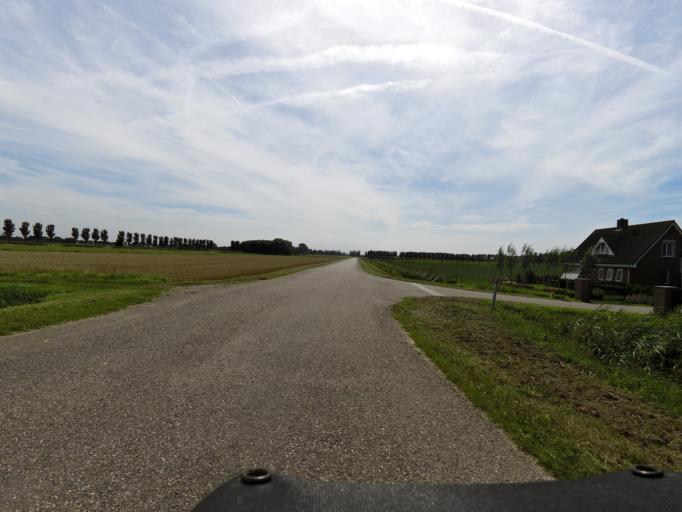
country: NL
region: South Holland
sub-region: Gemeente Goeree-Overflakkee
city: Dirksland
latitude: 51.7704
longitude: 4.1069
